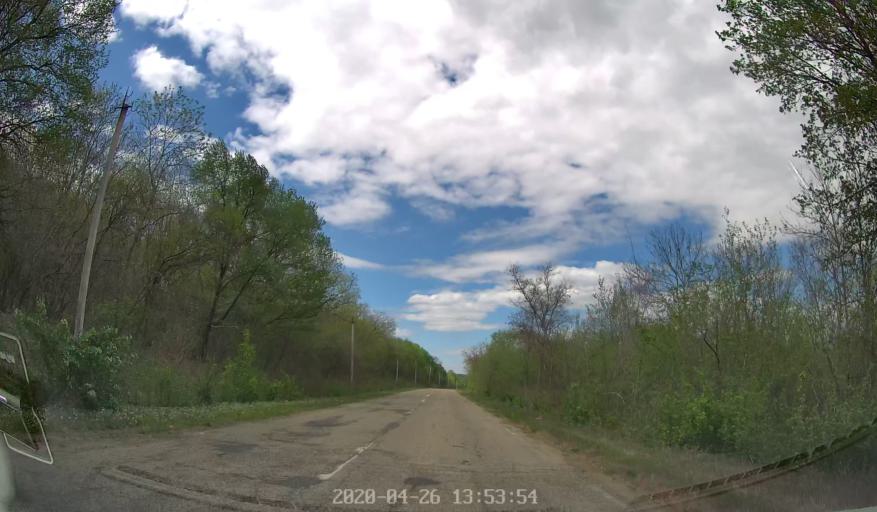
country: MD
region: Telenesti
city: Cocieri
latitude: 47.2823
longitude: 29.1051
